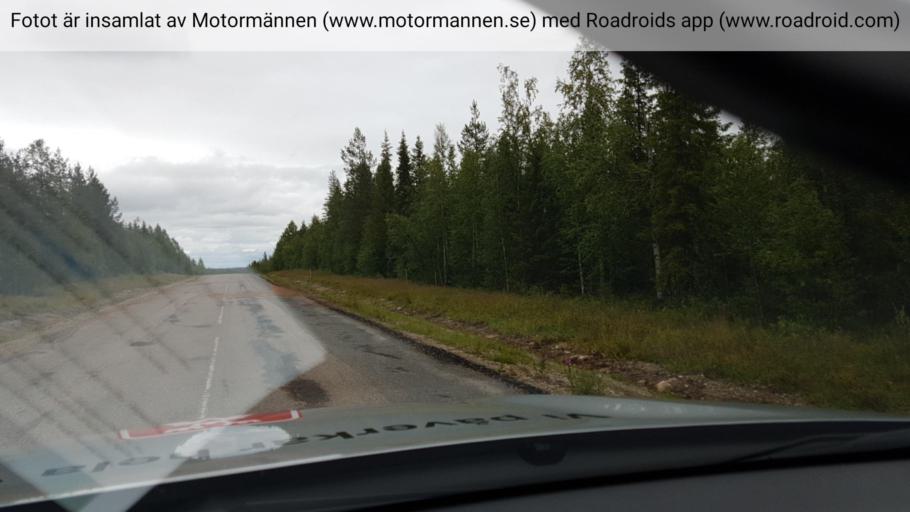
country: SE
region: Norrbotten
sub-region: Overkalix Kommun
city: OEverkalix
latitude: 67.0552
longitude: 22.1901
